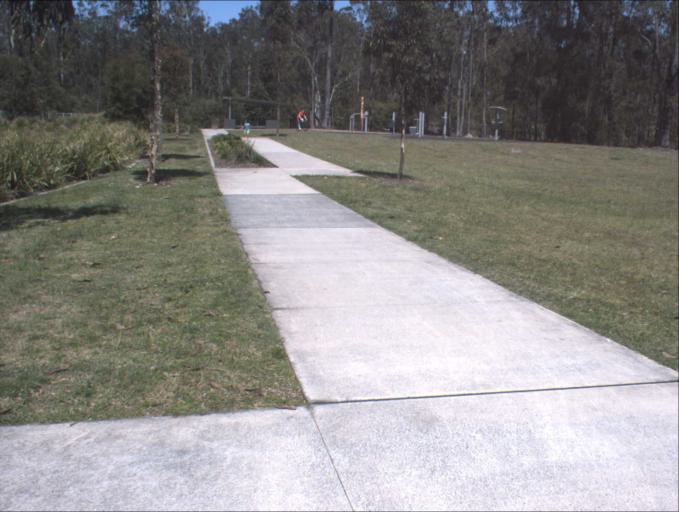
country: AU
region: Queensland
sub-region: Logan
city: Waterford West
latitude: -27.7162
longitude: 153.1469
